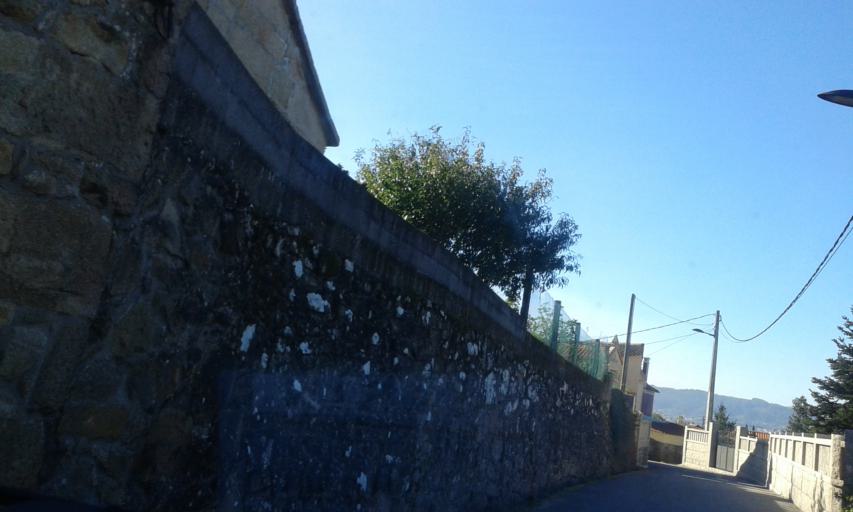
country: ES
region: Galicia
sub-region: Provincia de Pontevedra
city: Bueu
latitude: 42.3508
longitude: -8.7483
